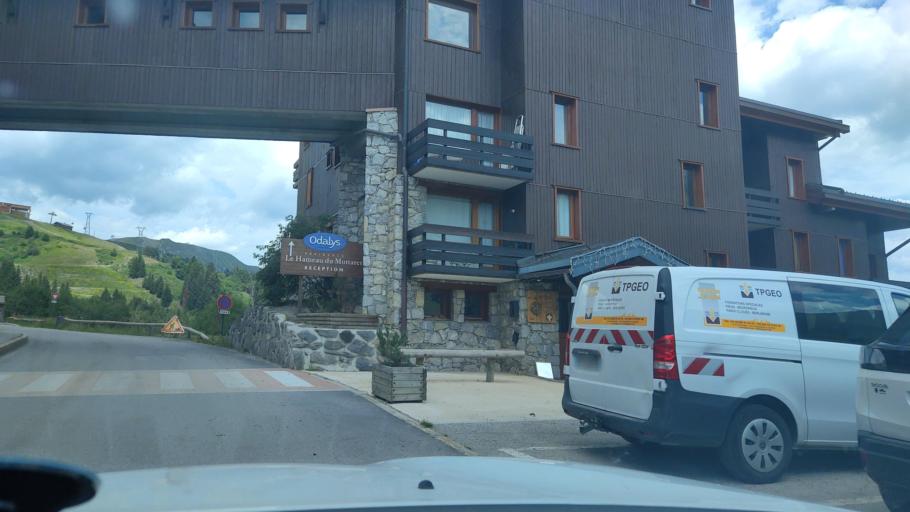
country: FR
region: Rhone-Alpes
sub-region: Departement de la Savoie
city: Meribel
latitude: 45.3741
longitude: 6.5731
